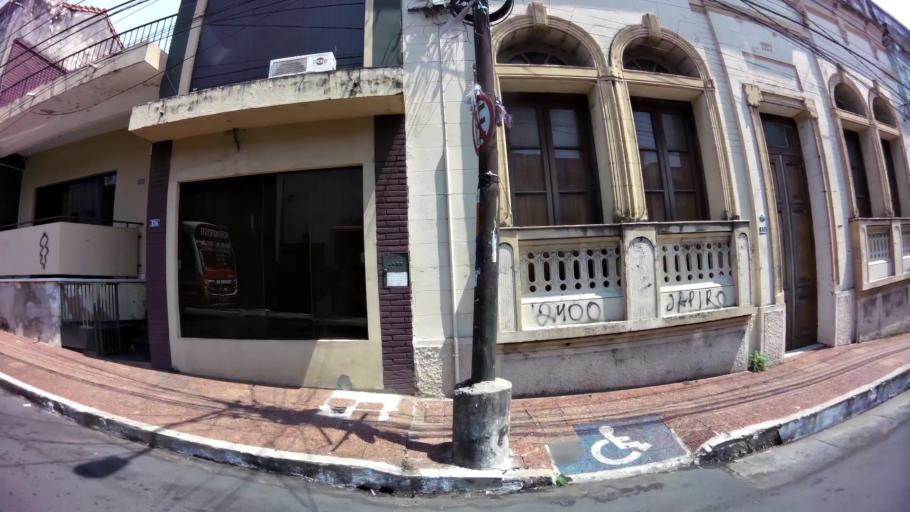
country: PY
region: Asuncion
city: Asuncion
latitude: -25.2832
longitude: -57.6428
